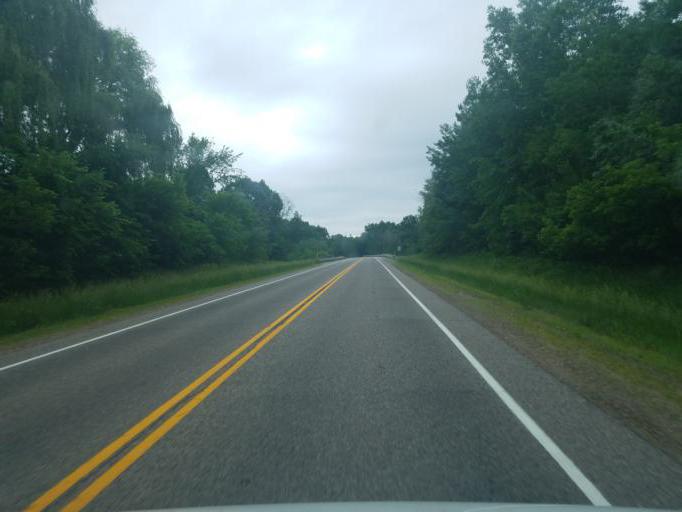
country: US
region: Wisconsin
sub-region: Juneau County
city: Elroy
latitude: 43.7779
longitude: -90.1991
